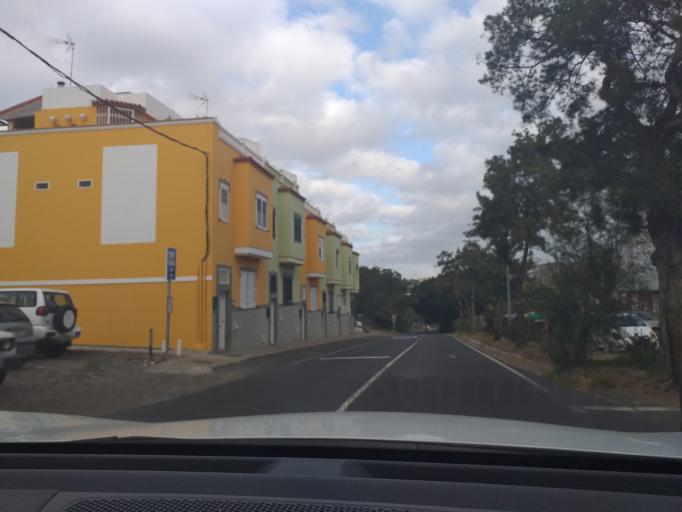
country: ES
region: Canary Islands
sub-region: Provincia de Las Palmas
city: Arucas
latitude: 28.0996
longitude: -15.4831
